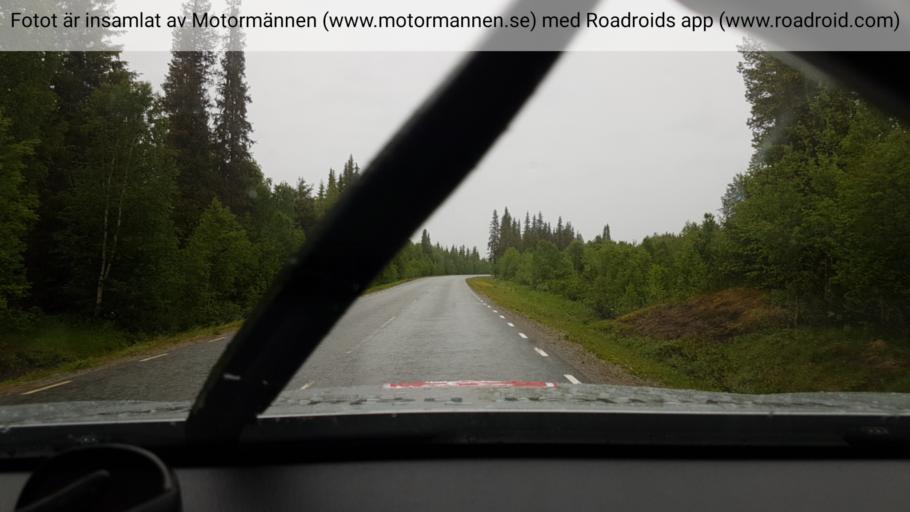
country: SE
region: Vaesterbotten
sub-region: Storumans Kommun
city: Fristad
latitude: 65.8944
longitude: 16.3431
